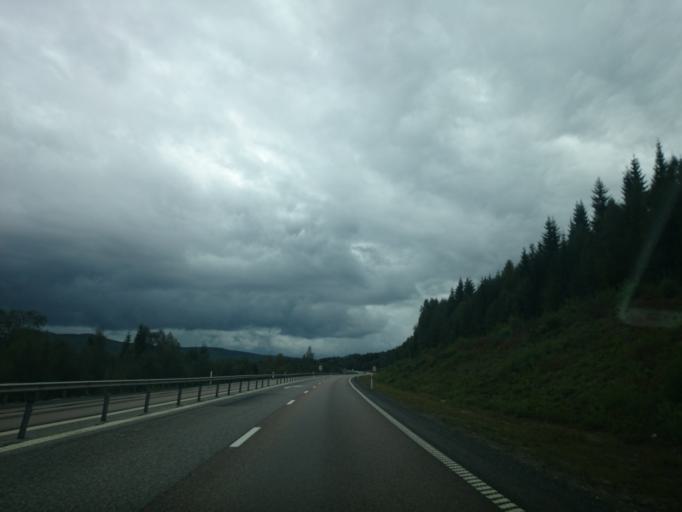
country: SE
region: Vaesternorrland
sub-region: Kramfors Kommun
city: Nordingra
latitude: 62.9895
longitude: 18.1631
